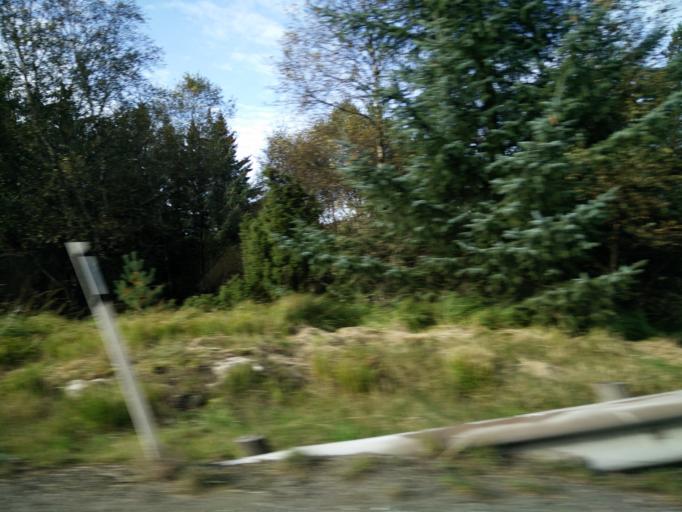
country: NO
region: Hordaland
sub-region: Sveio
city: Sveio
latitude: 59.5309
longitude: 5.3308
